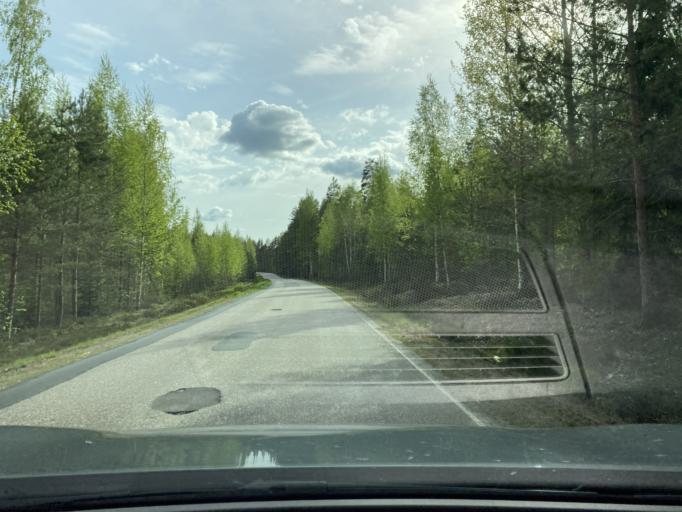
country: FI
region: Varsinais-Suomi
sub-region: Salo
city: Kiikala
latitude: 60.4803
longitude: 23.5365
